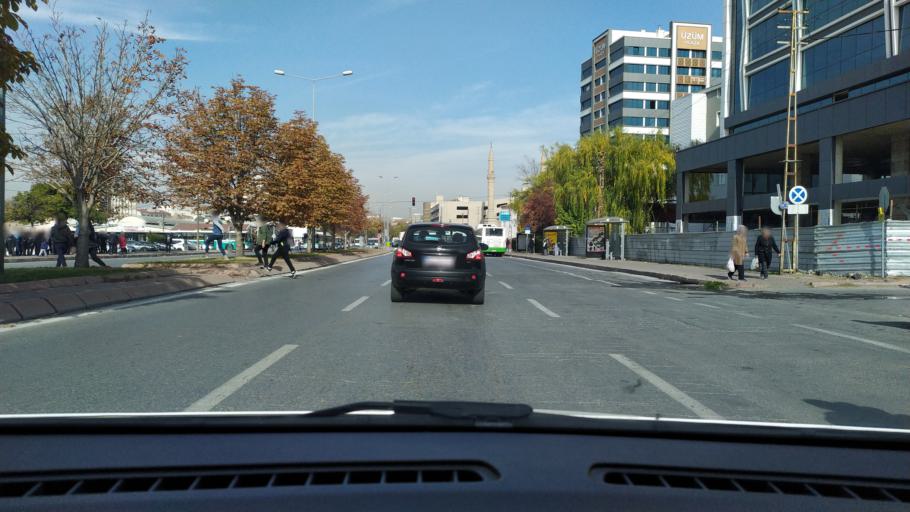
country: TR
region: Kayseri
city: Kayseri
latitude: 38.7132
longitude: 35.4913
